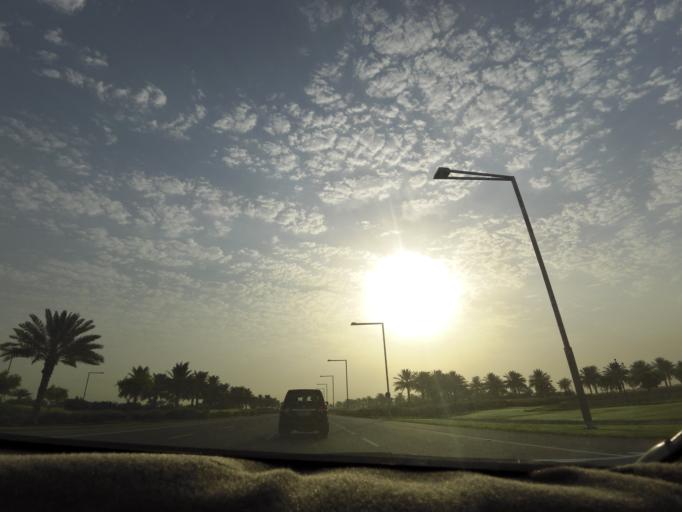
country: QA
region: Al Wakrah
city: Al Wakrah
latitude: 25.2427
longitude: 51.5966
